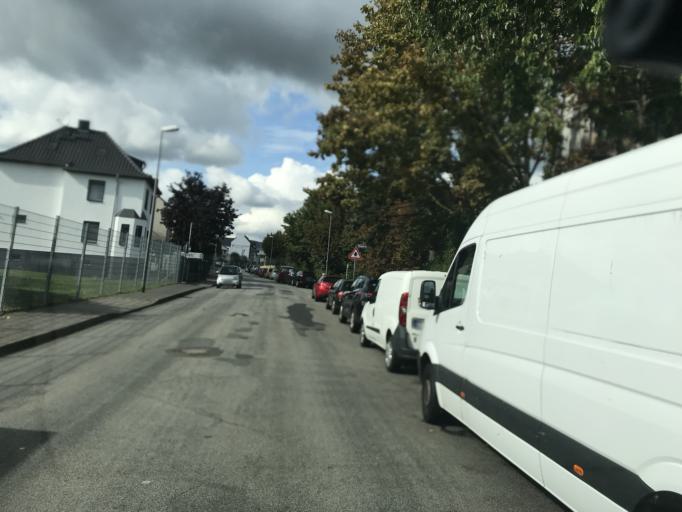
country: DE
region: Hesse
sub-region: Regierungsbezirk Darmstadt
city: Wiesbaden
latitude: 50.0743
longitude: 8.2099
